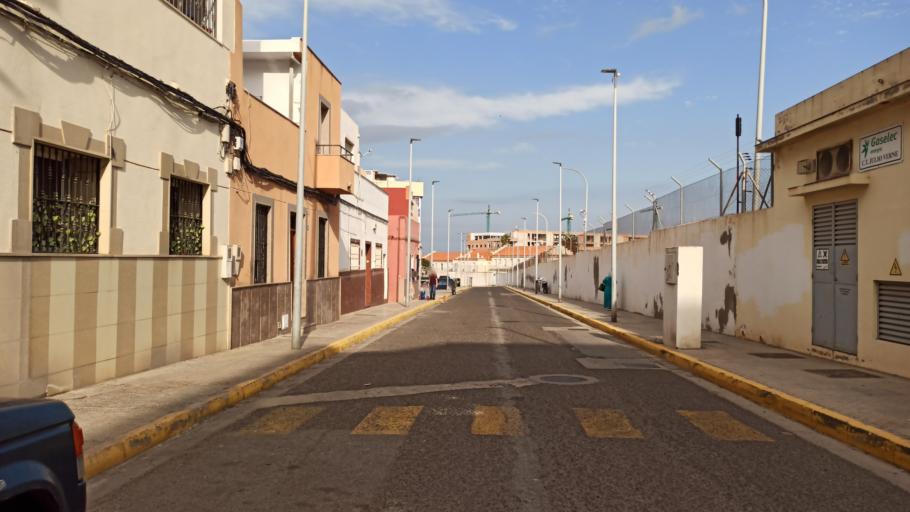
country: ES
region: Melilla
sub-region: Melilla
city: Melilla
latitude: 35.2826
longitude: -2.9475
